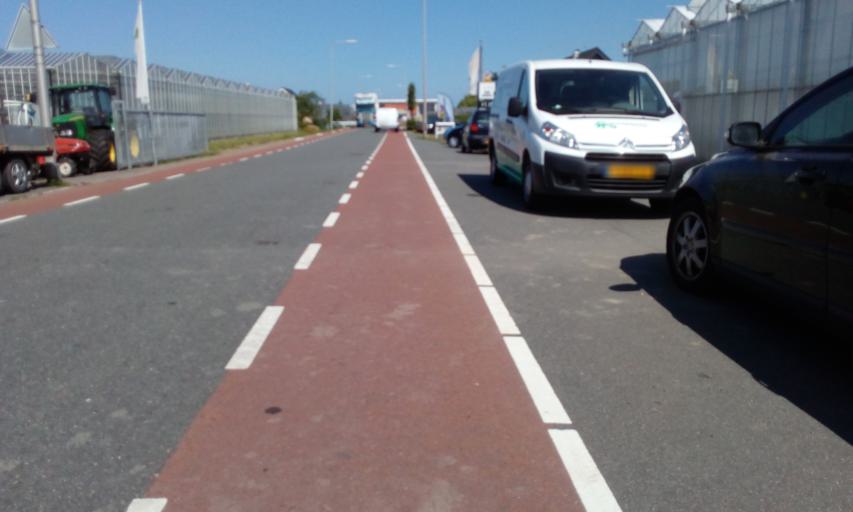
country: NL
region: South Holland
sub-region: Gemeente Westland
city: De Lier
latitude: 51.9691
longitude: 4.2443
